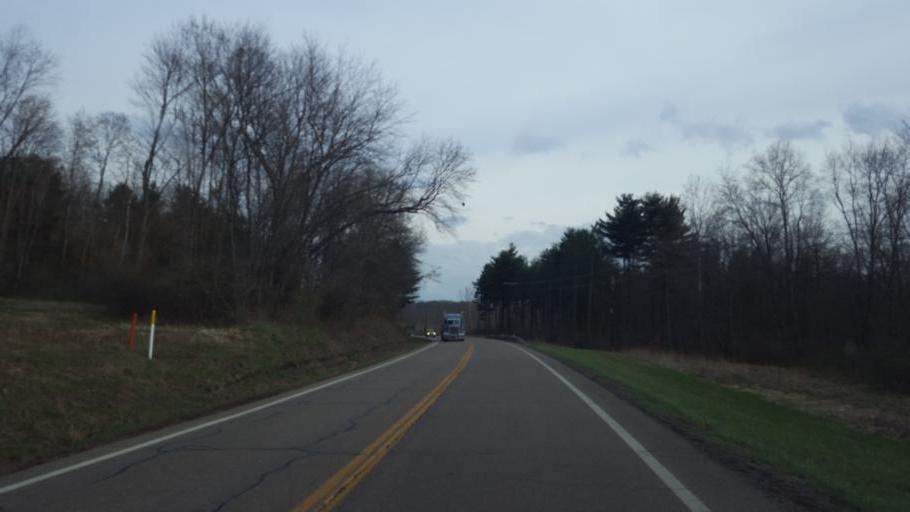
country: US
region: Ohio
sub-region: Coshocton County
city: Coshocton
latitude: 40.1897
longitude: -81.8408
